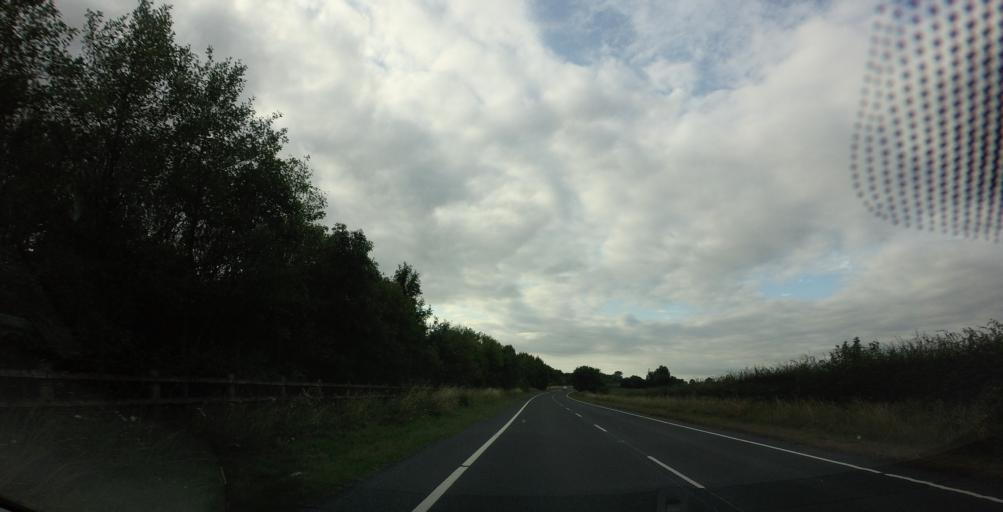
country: GB
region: England
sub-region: North Yorkshire
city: Boroughbridge
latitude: 54.0549
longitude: -1.3879
